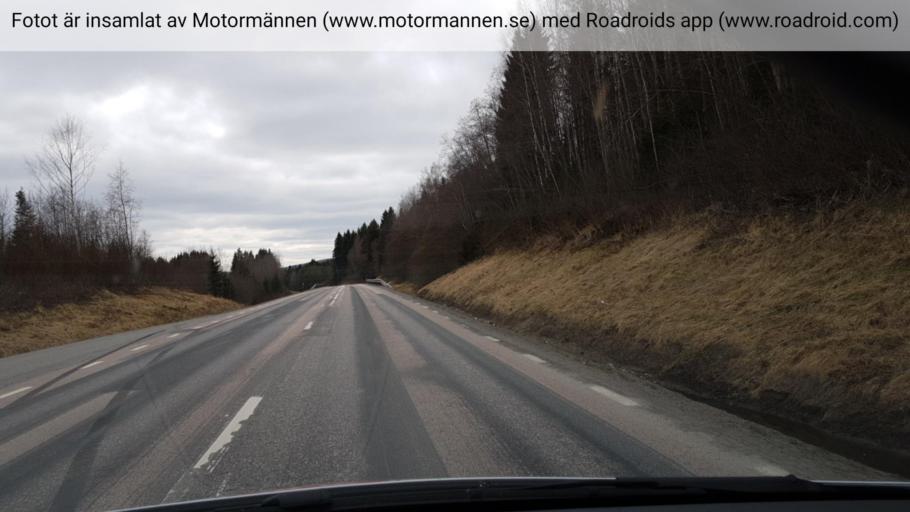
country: SE
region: Vaesternorrland
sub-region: OErnskoeldsviks Kommun
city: Ornskoldsvik
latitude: 63.3630
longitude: 18.6530
